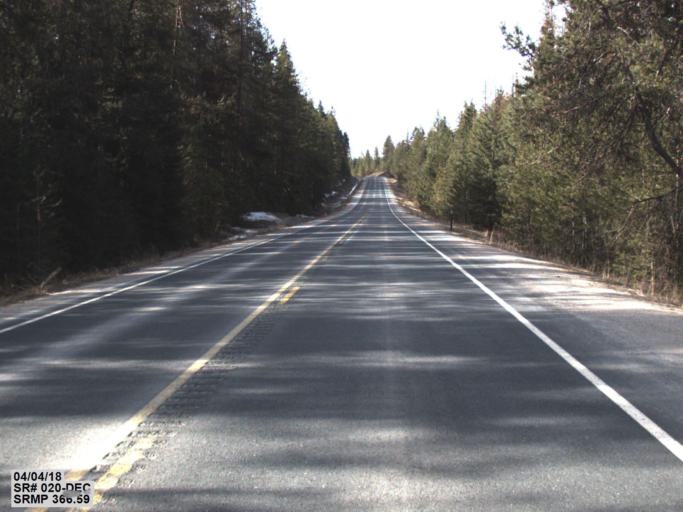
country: US
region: Washington
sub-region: Stevens County
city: Colville
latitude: 48.5182
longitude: -117.6946
